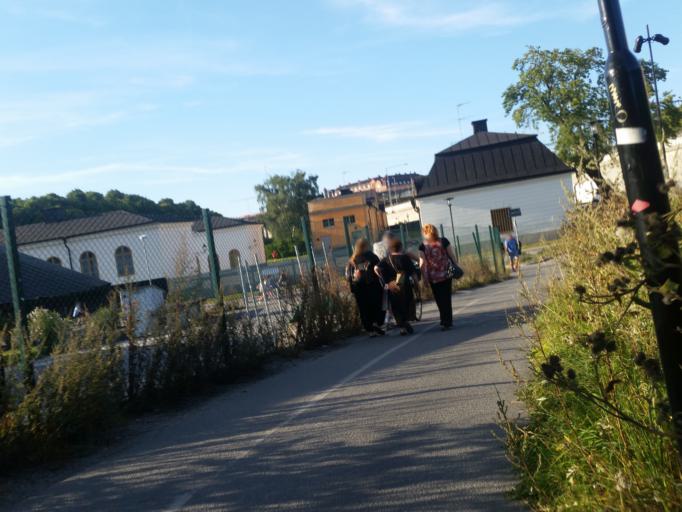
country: SE
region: Stockholm
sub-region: Solna Kommun
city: Solna
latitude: 59.3403
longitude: 18.0254
